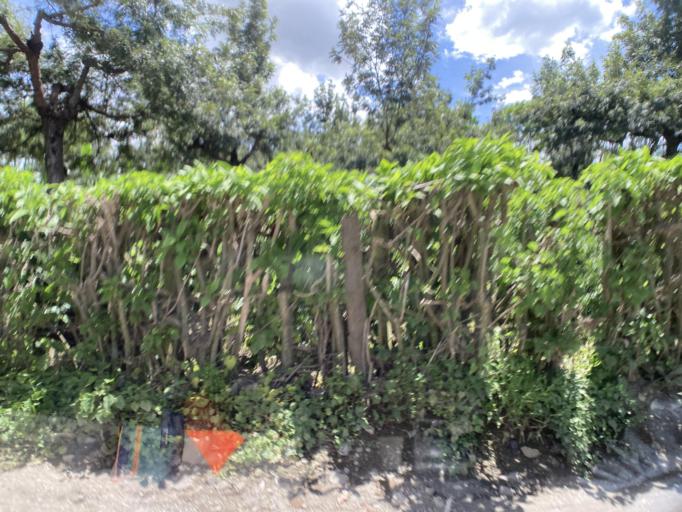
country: GT
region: Sacatepequez
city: Antigua Guatemala
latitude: 14.5425
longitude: -90.7353
